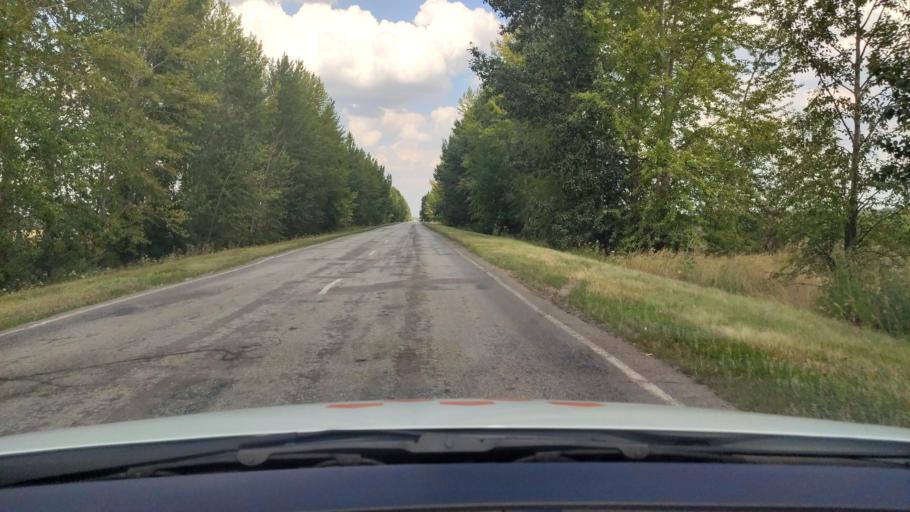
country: RU
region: Voronezj
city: Pereleshinskiy
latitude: 51.7294
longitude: 40.3771
